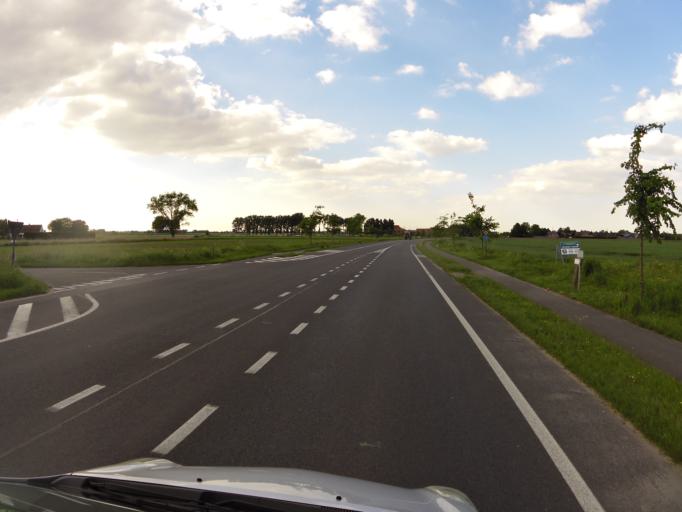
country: BE
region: Flanders
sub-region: Provincie West-Vlaanderen
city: Diksmuide
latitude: 51.0749
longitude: 2.8747
